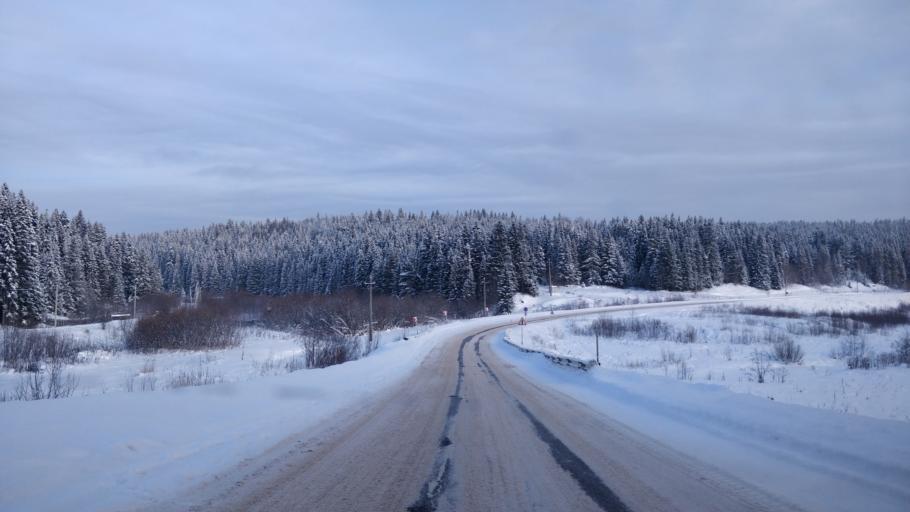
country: RU
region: Perm
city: Polazna
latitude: 58.3091
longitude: 56.4610
